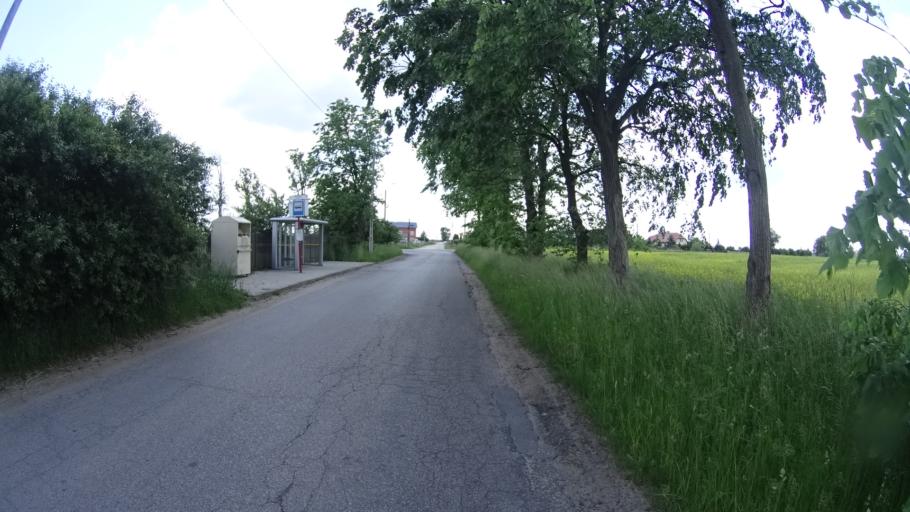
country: PL
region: Masovian Voivodeship
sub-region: Powiat piaseczynski
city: Tarczyn
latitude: 52.0326
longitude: 20.8224
